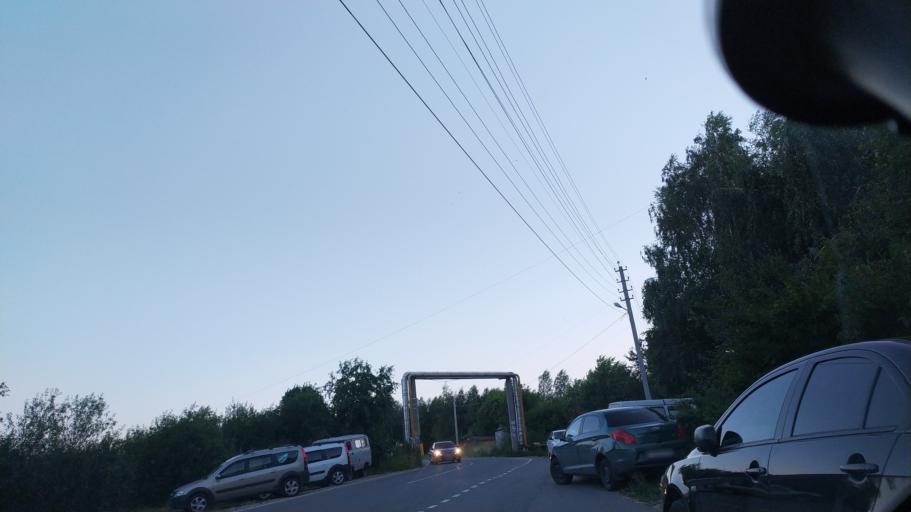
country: RU
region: Chuvashia
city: Ishley
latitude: 56.1250
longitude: 47.0420
